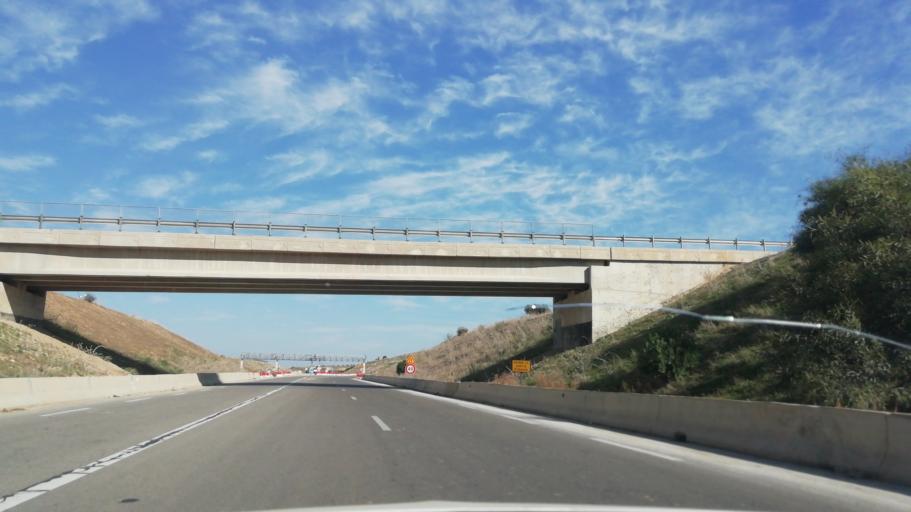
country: DZ
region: Tlemcen
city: Bensekrane
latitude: 34.9818
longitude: -1.2208
